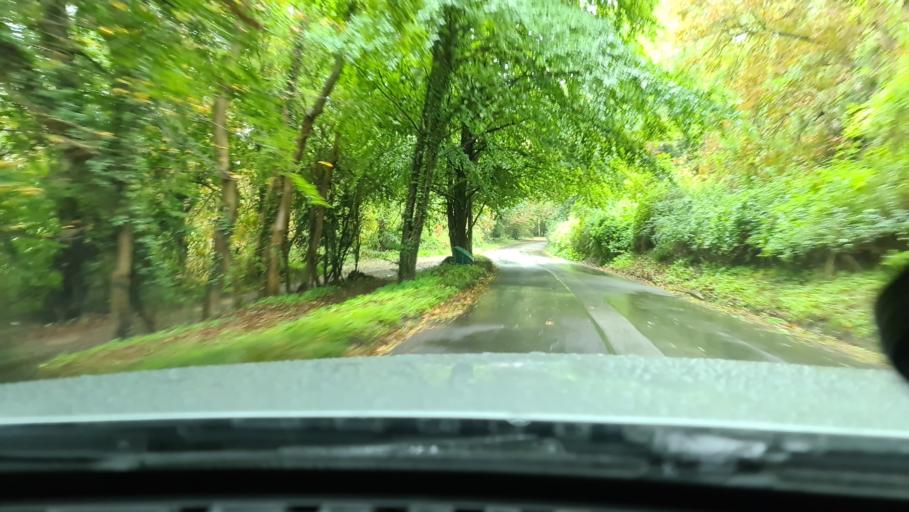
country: GB
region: England
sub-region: Oxfordshire
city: Somerton
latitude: 51.9212
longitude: -1.3056
